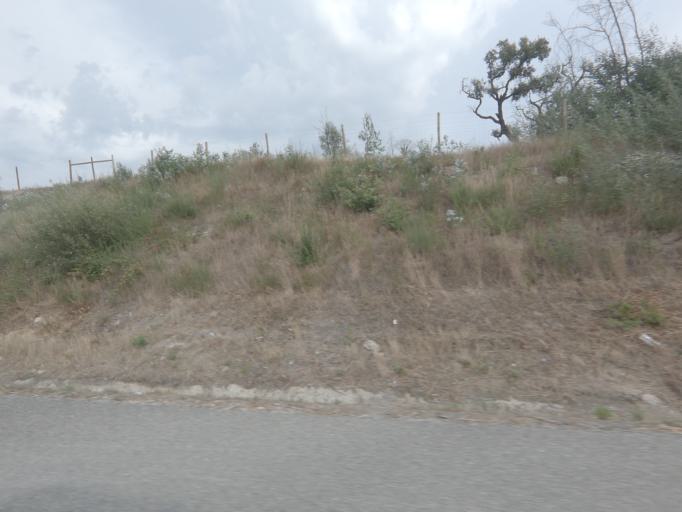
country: PT
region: Viseu
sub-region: Santa Comba Dao
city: Santa Comba Dao
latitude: 40.4242
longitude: -8.1189
